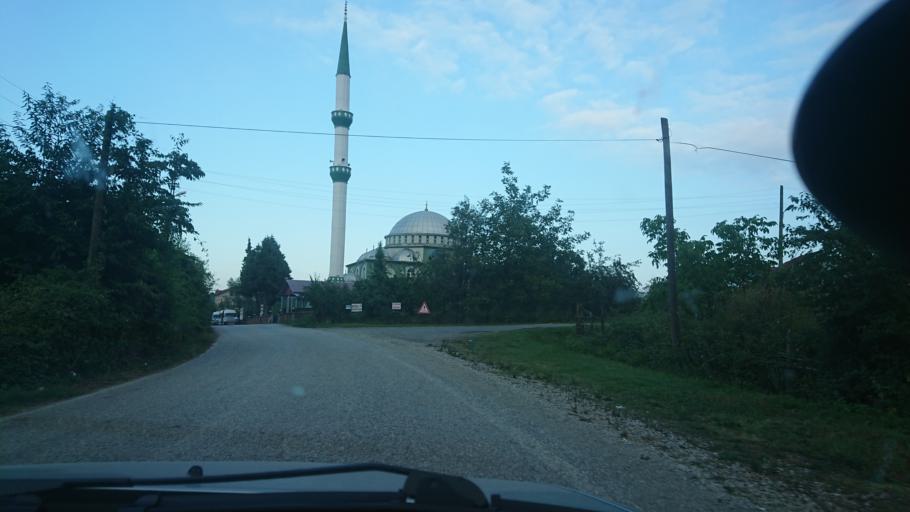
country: TR
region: Samsun
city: Tekkekoy
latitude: 41.1725
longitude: 36.5382
